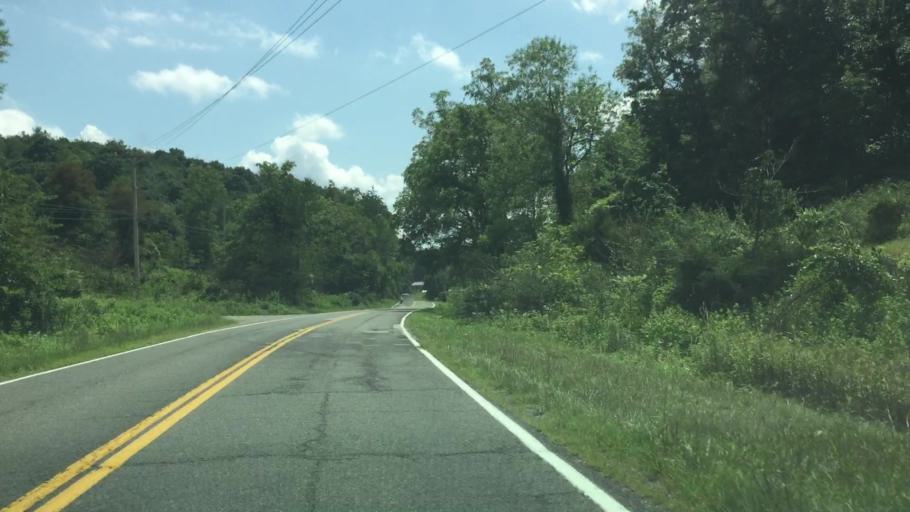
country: US
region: Virginia
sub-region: Pulaski County
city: Pulaski
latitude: 37.0364
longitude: -80.7235
